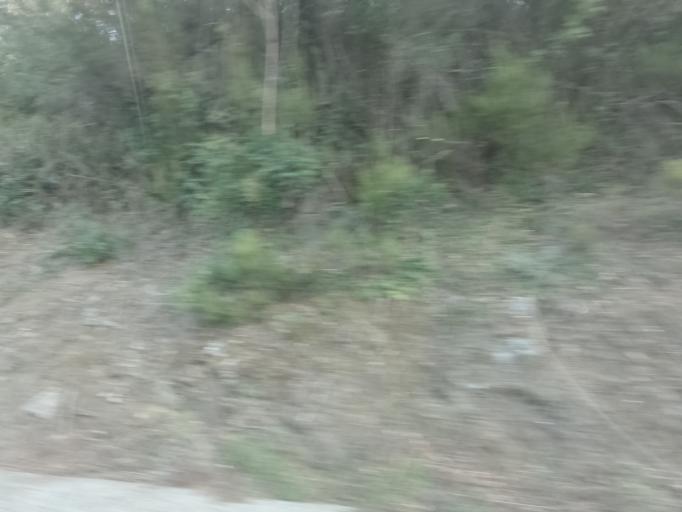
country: PT
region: Vila Real
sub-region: Sabrosa
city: Sabrosa
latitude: 41.2652
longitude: -7.5532
